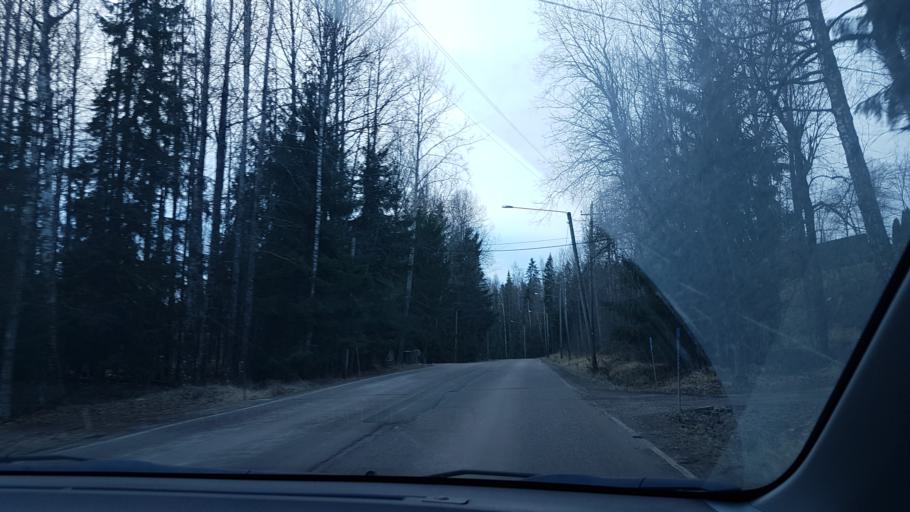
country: FI
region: Uusimaa
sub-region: Helsinki
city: Kauniainen
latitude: 60.3402
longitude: 24.7117
